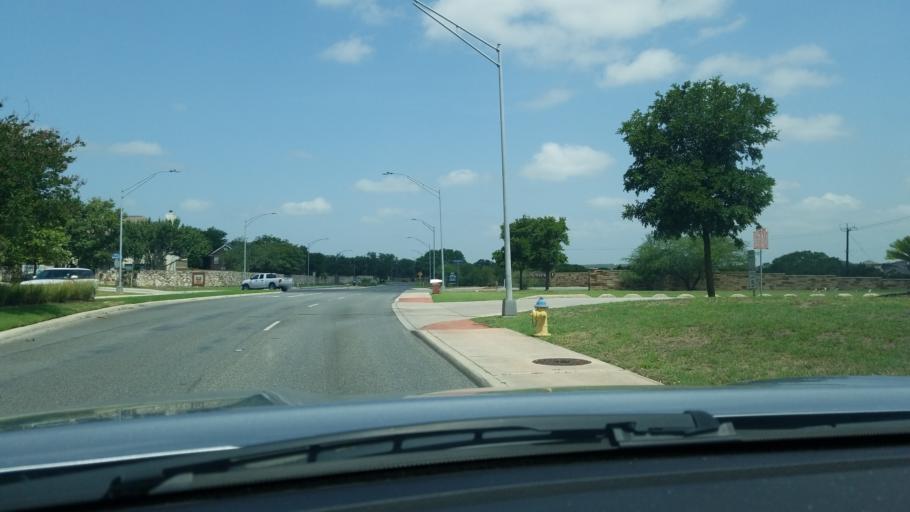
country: US
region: Texas
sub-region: Bexar County
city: Hollywood Park
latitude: 29.6452
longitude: -98.4923
